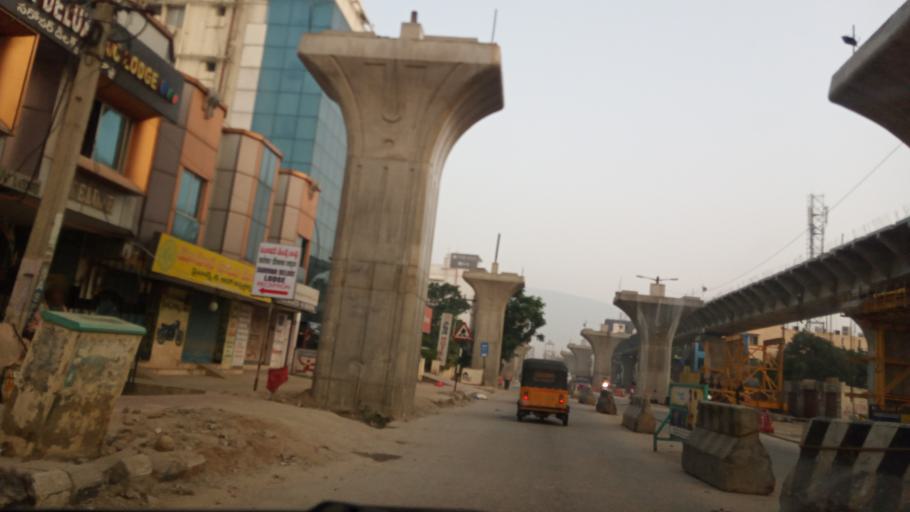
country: IN
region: Andhra Pradesh
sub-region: Chittoor
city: Tirupati
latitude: 13.6343
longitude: 79.4278
